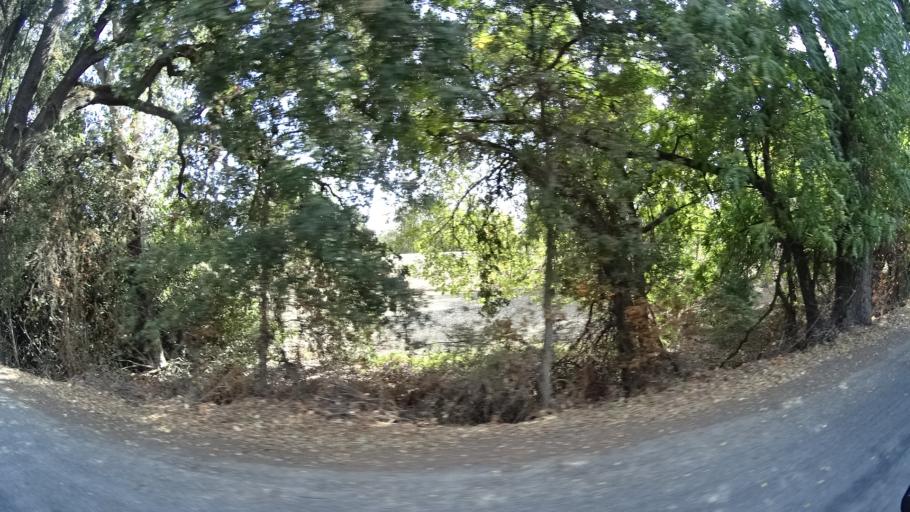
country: US
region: California
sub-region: Yolo County
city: Woodland
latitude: 38.7718
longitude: -121.6913
